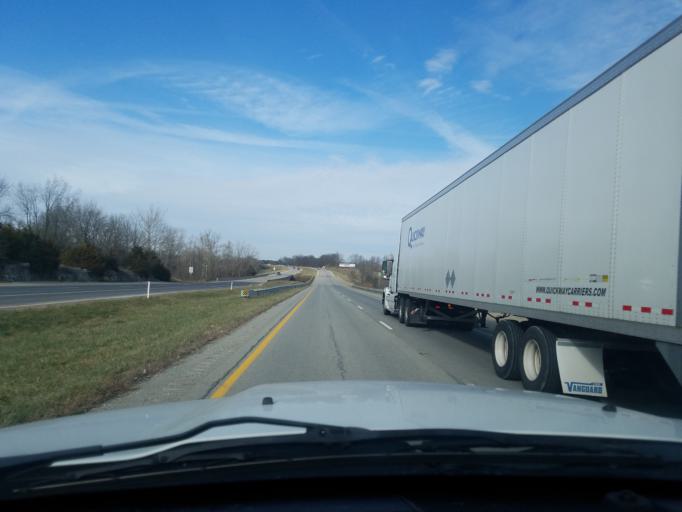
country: US
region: Indiana
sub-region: Monroe County
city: Bloomington
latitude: 39.0947
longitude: -86.5461
